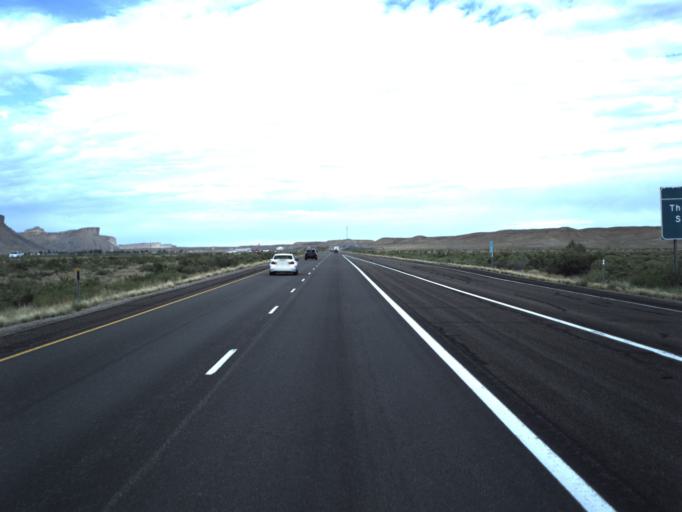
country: US
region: Utah
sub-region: Grand County
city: Moab
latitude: 38.9558
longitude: -109.7488
